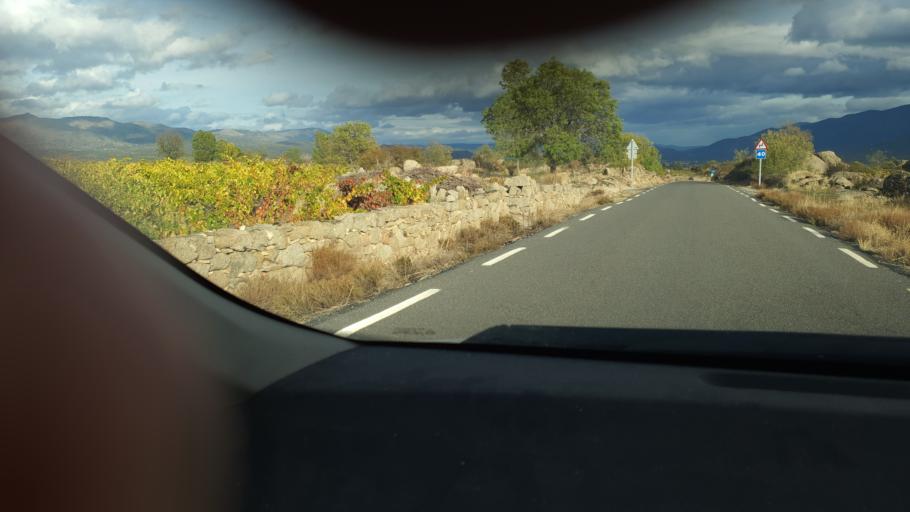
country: ES
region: Castille and Leon
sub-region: Provincia de Avila
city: Burgohondo
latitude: 40.4098
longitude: -4.8174
